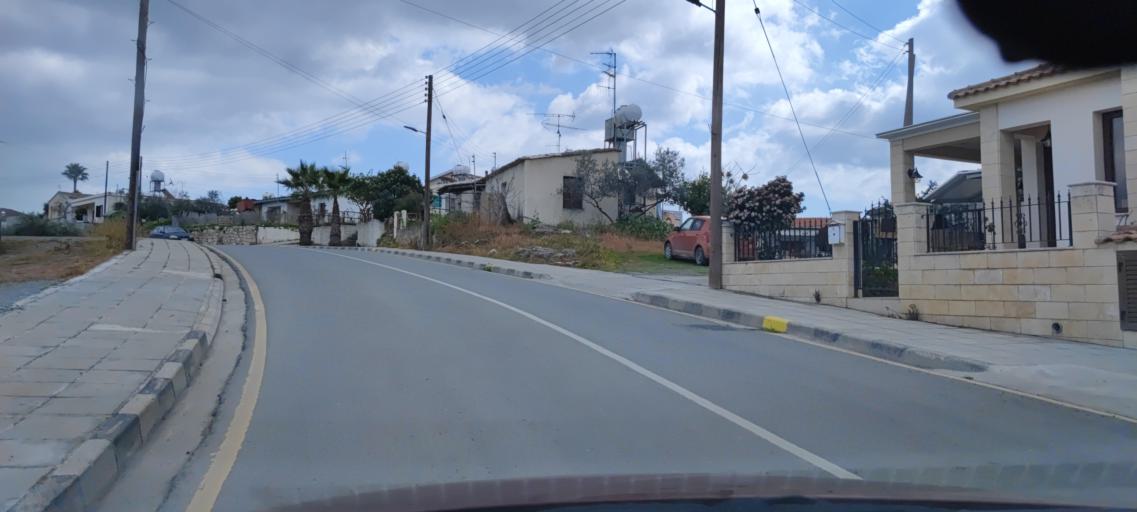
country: CY
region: Larnaka
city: Kornos
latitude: 34.9205
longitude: 33.3977
